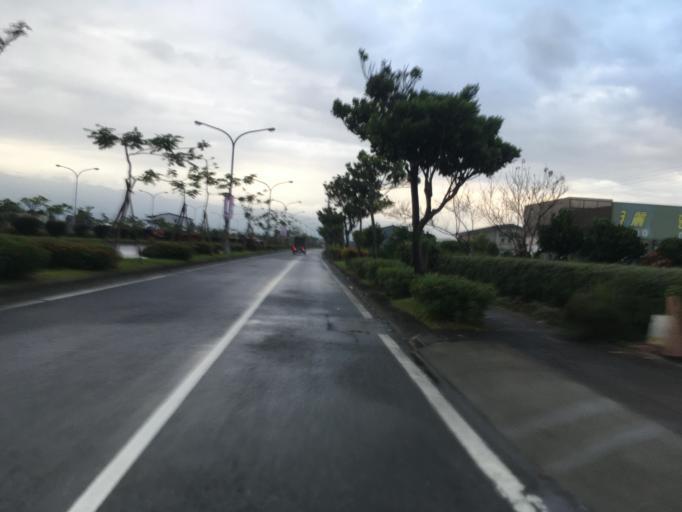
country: TW
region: Taiwan
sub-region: Yilan
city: Yilan
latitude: 24.7275
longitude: 121.7722
